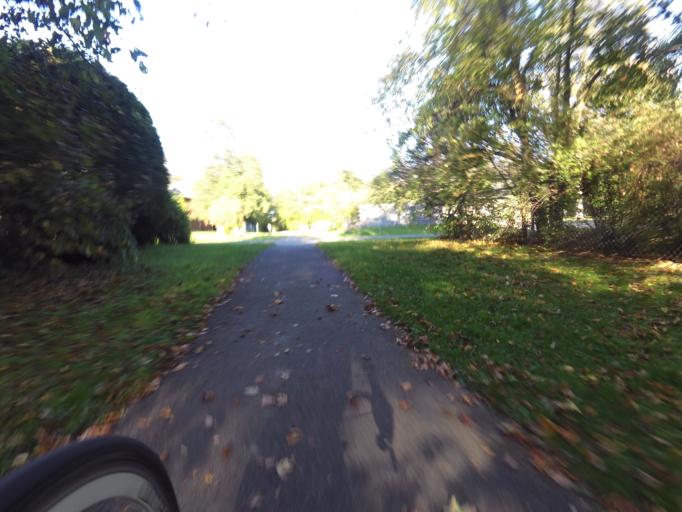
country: CA
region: Ontario
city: Bells Corners
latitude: 45.2187
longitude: -75.6918
